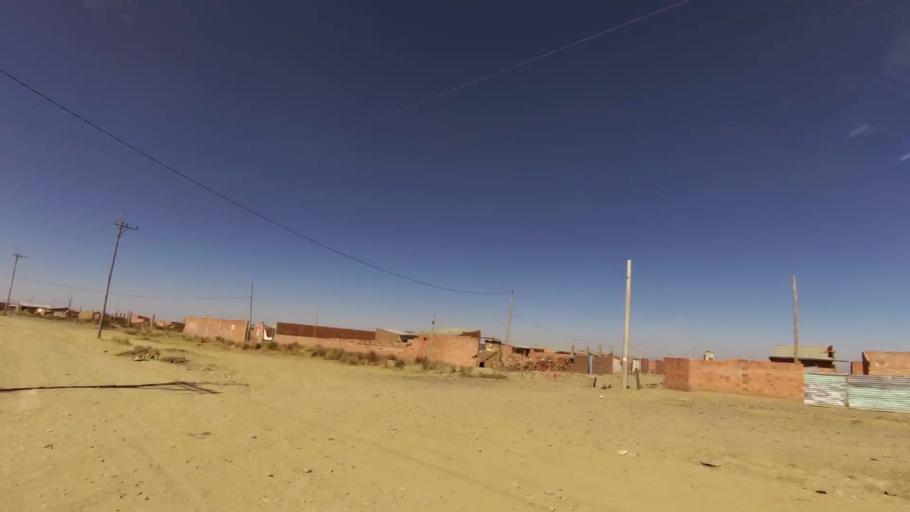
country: BO
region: La Paz
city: La Paz
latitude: -16.5858
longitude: -68.2123
